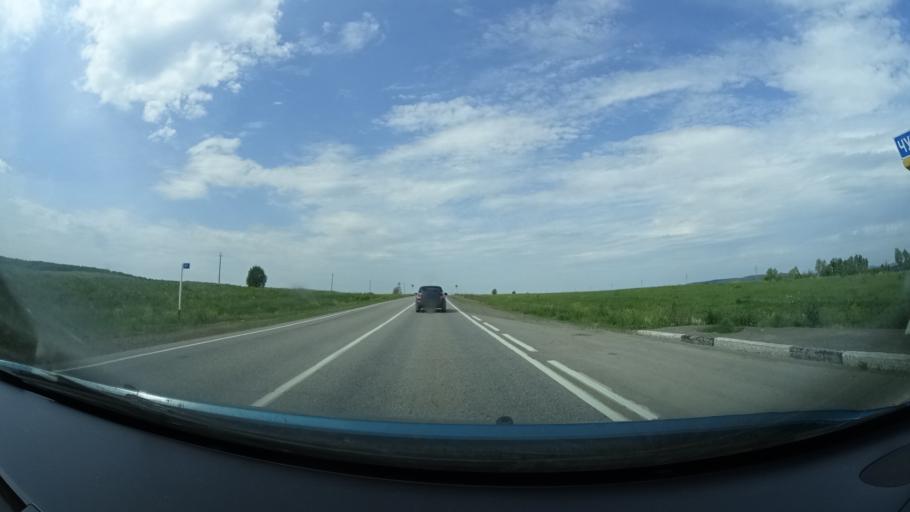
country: RU
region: Perm
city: Barda
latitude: 57.0321
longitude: 55.5496
